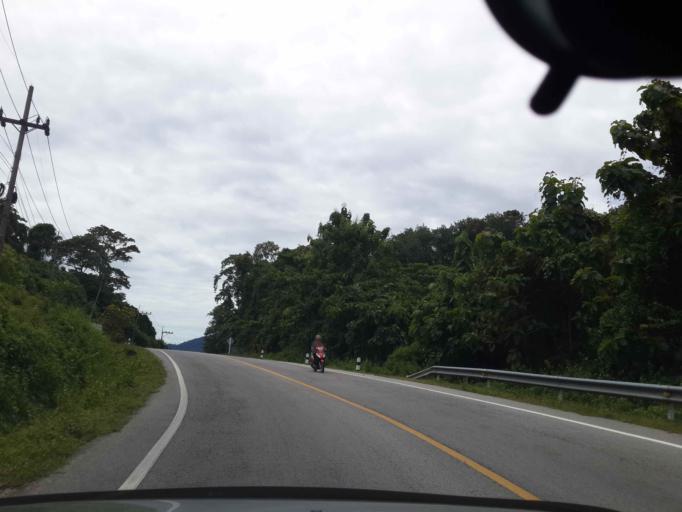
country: TH
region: Narathiwat
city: Rueso
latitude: 6.3619
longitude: 101.5546
